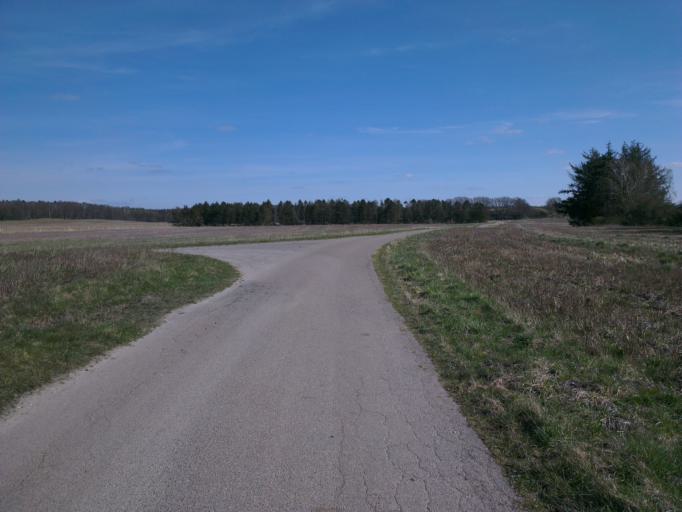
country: DK
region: Capital Region
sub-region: Frederikssund Kommune
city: Jaegerspris
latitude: 55.8956
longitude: 11.9784
